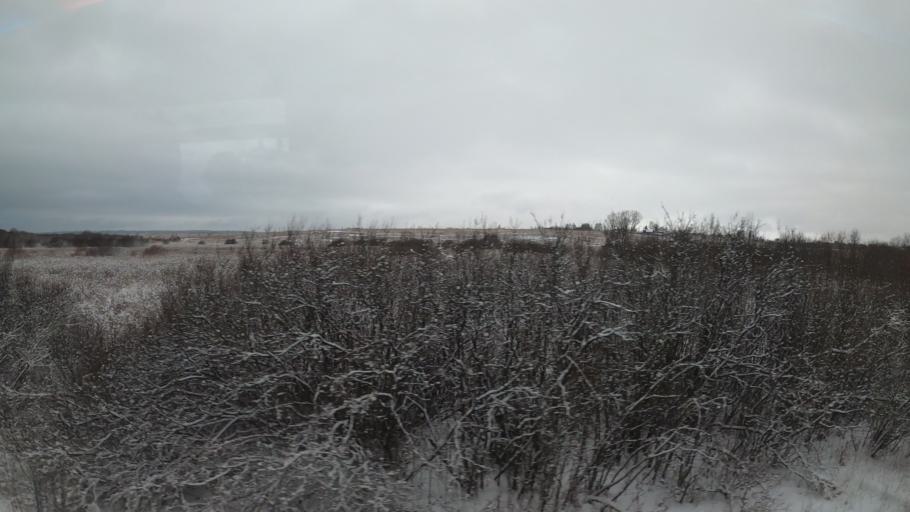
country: RU
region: Jaroslavl
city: Pereslavl'-Zalesskiy
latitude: 56.6954
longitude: 38.9171
